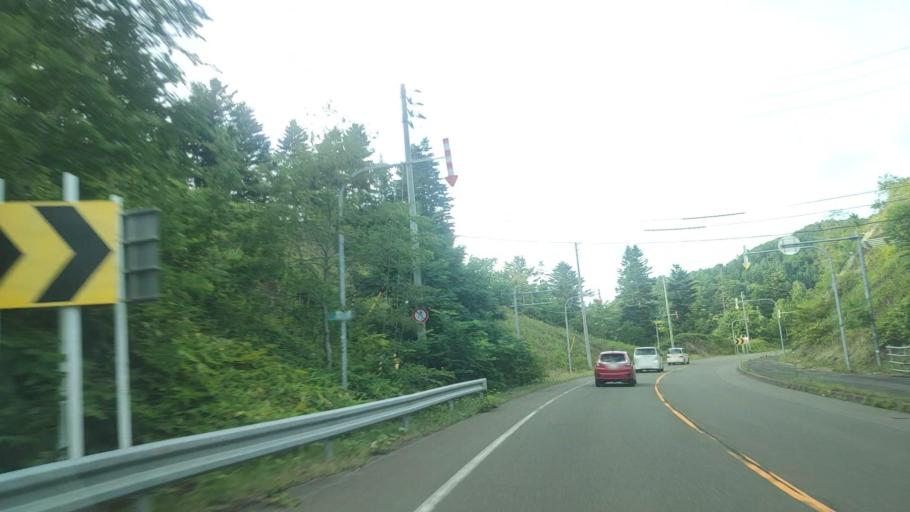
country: JP
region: Hokkaido
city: Iwamizawa
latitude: 43.0263
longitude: 141.9537
